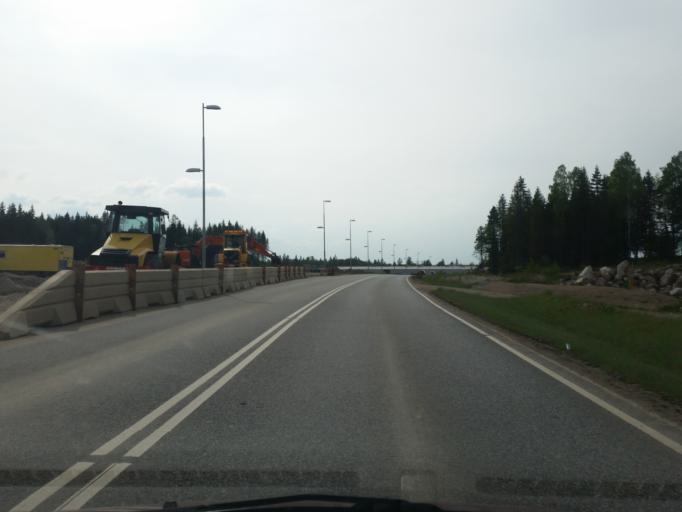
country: SE
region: Vaestra Goetaland
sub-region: Ulricehamns Kommun
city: Ulricehamn
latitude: 57.8031
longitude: 13.4670
